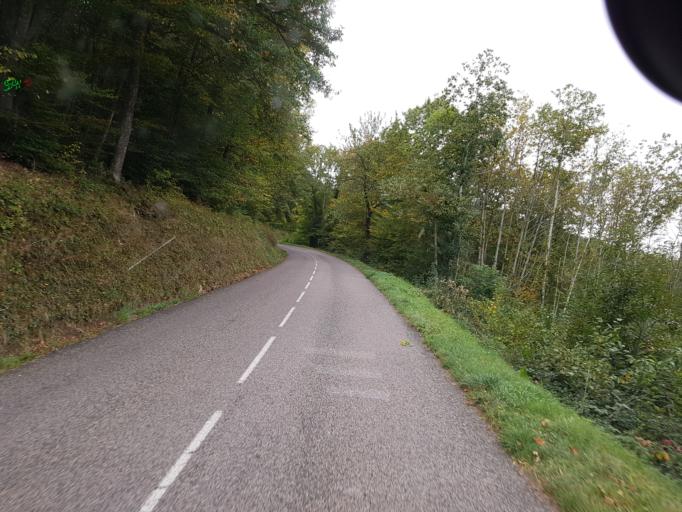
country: FR
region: Rhone-Alpes
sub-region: Departement du Rhone
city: Aveize
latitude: 45.6712
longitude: 4.4386
